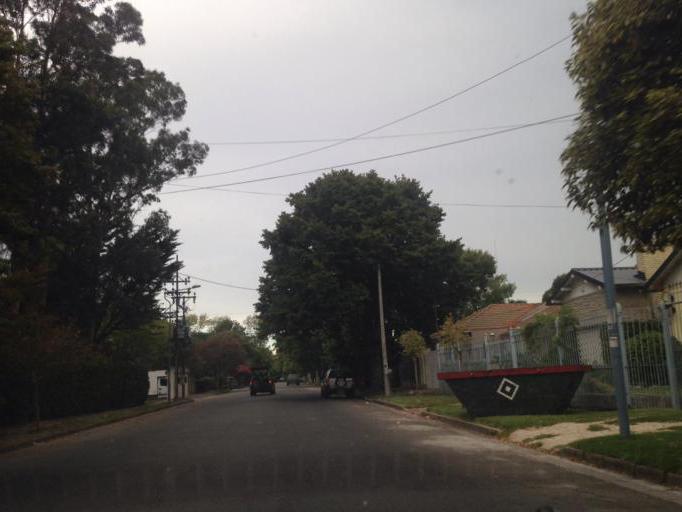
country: AR
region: Buenos Aires
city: Mar del Plata
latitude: -38.0260
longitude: -57.5454
